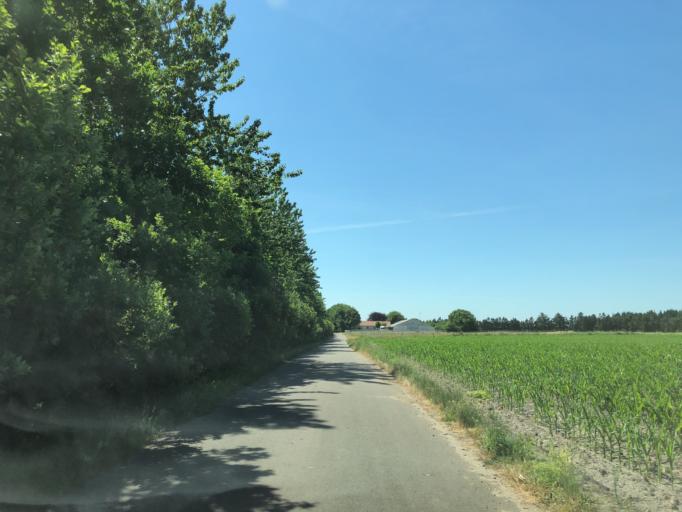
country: DK
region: Central Jutland
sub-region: Struer Kommune
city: Struer
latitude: 56.4335
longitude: 8.4442
